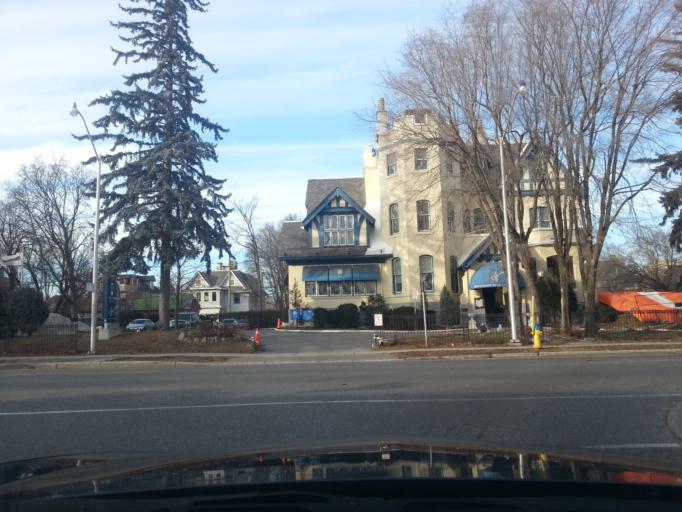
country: CA
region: Ontario
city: Ottawa
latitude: 45.4287
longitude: -75.6745
